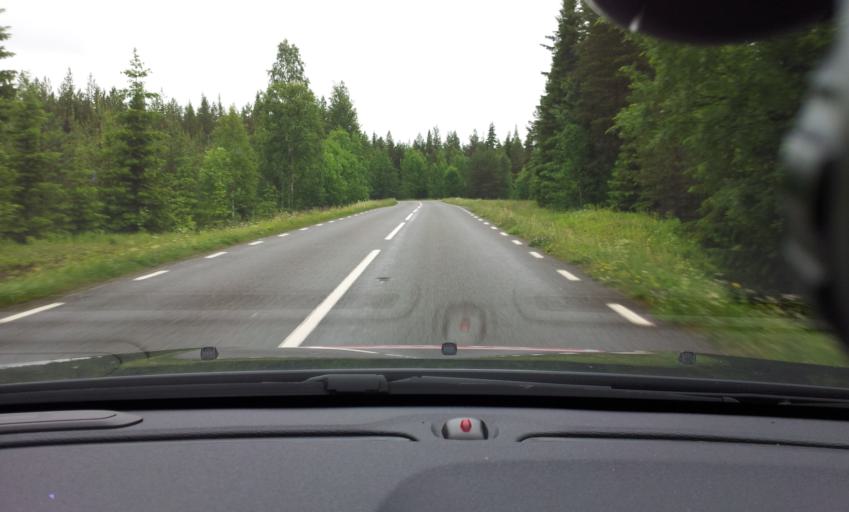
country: SE
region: Jaemtland
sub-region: Stroemsunds Kommun
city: Stroemsund
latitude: 63.4815
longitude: 15.4445
